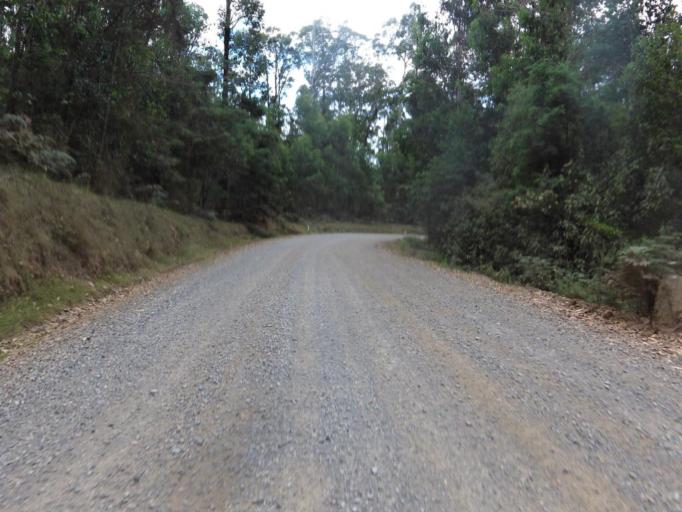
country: AU
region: Victoria
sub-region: Yarra Ranges
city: Healesville
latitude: -37.4059
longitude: 145.5586
